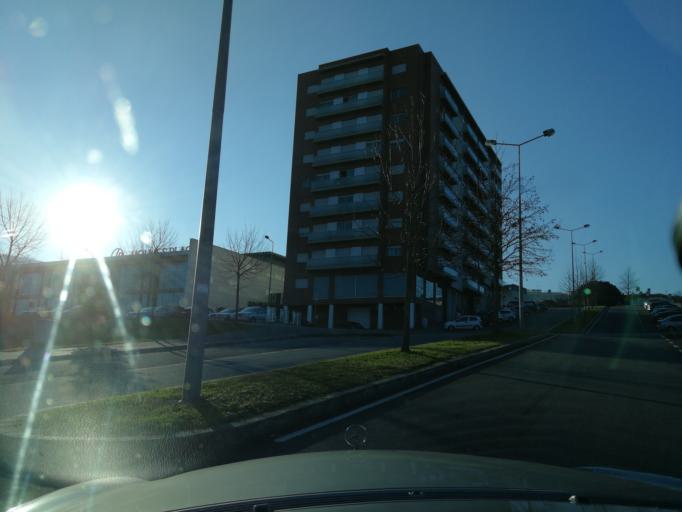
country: PT
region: Braga
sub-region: Braga
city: Braga
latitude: 41.5377
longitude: -8.4035
